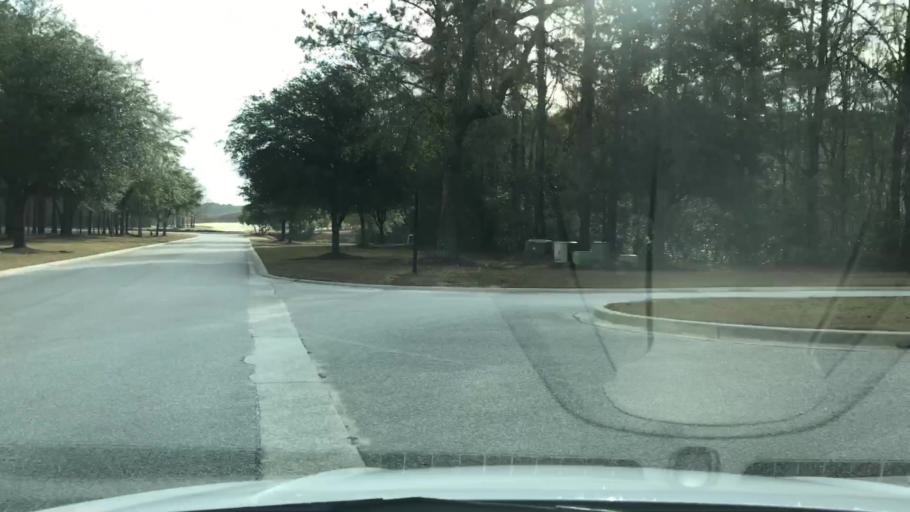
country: US
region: South Carolina
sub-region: Charleston County
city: Isle of Palms
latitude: 32.9063
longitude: -79.7199
